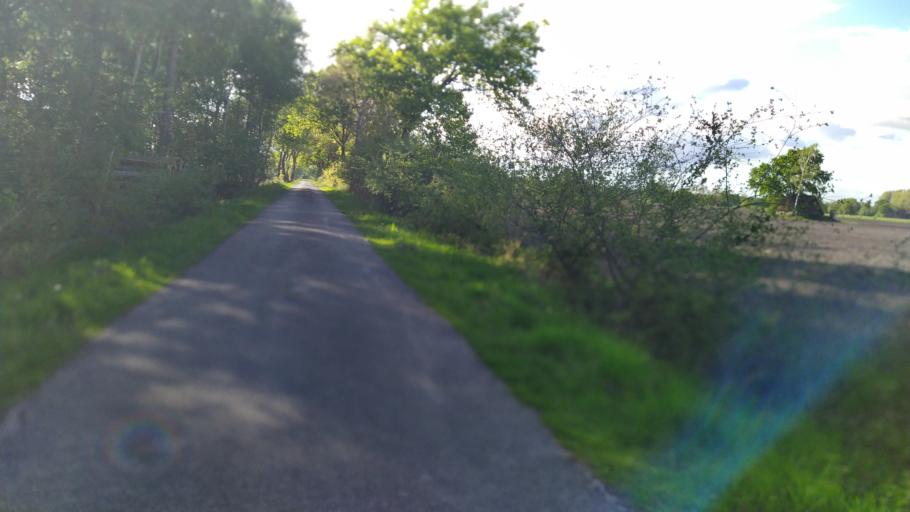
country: DE
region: Lower Saxony
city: Farven
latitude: 53.4053
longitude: 9.3437
